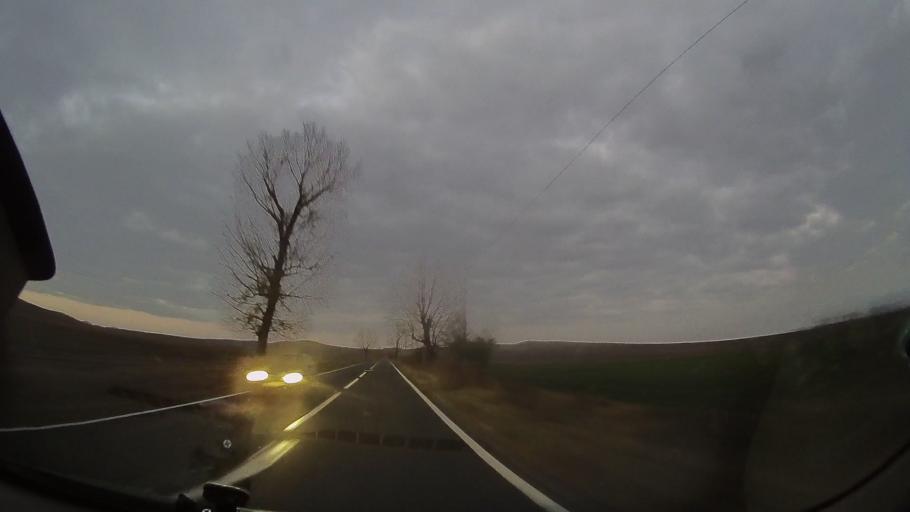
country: RO
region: Tulcea
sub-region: Comuna Nalbant
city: Nicolae Balcescu
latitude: 45.0034
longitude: 28.5969
